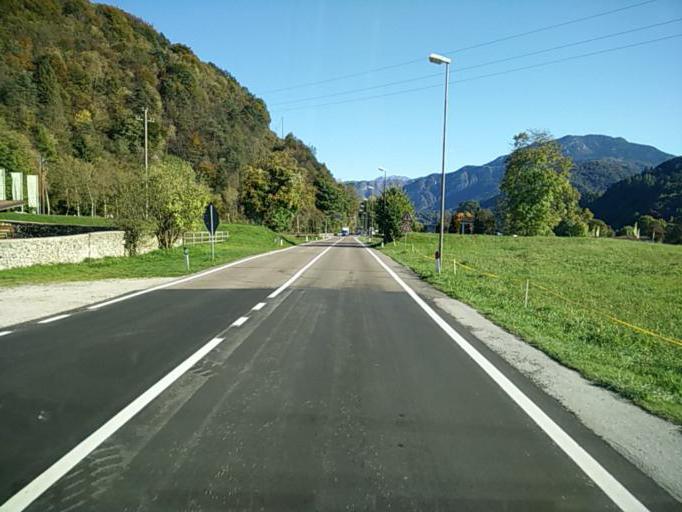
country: IT
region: Trentino-Alto Adige
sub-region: Provincia di Trento
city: Pieve di Ledro
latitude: 45.8881
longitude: 10.7327
